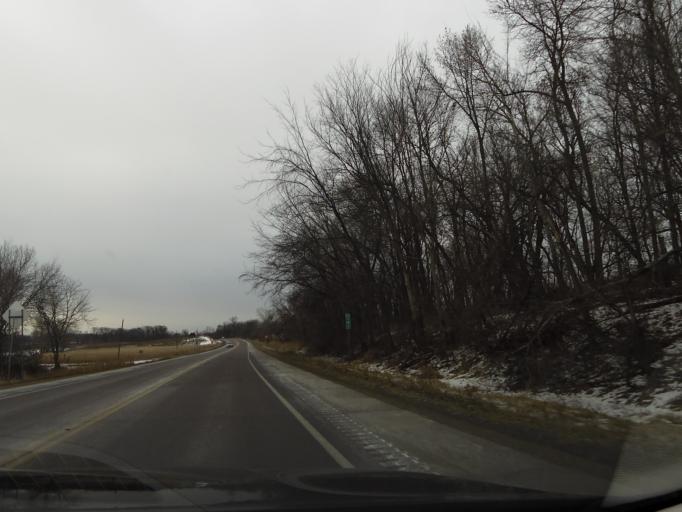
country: US
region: Minnesota
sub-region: Carver County
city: Cologne
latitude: 44.7762
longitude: -93.7362
